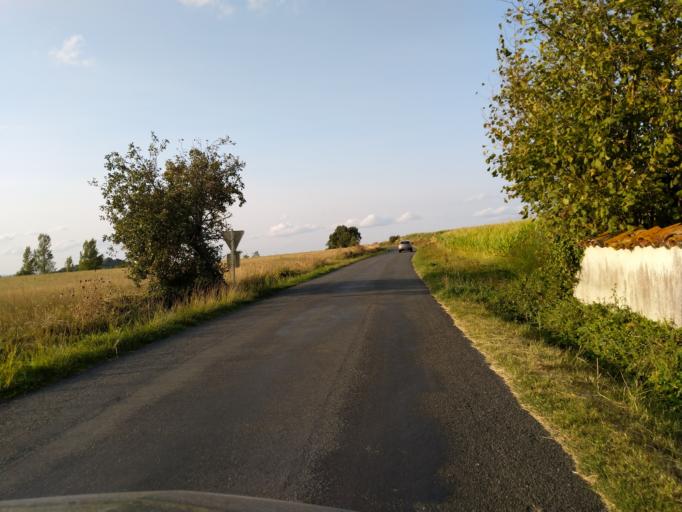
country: FR
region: Midi-Pyrenees
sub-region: Departement du Tarn
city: Frejairolles
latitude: 43.8675
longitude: 2.2333
